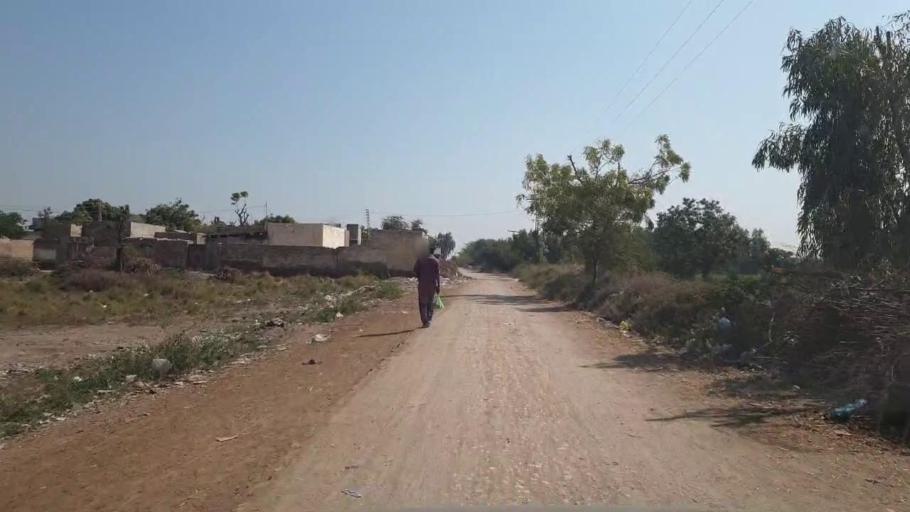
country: PK
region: Sindh
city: Digri
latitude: 25.2102
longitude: 69.1941
